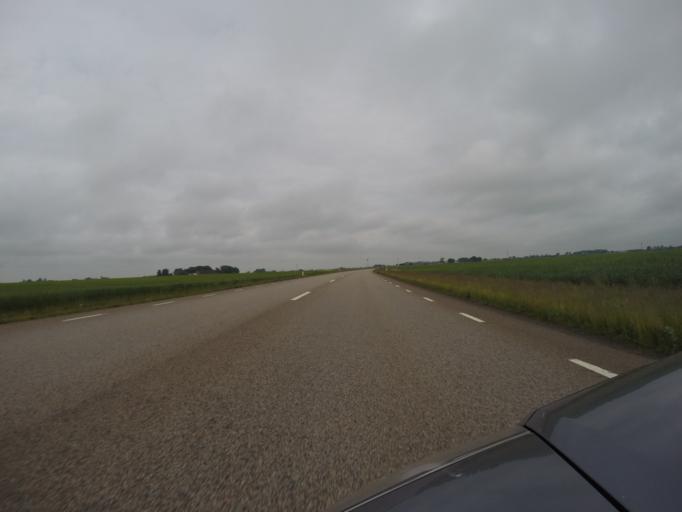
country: SE
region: Skane
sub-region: Helsingborg
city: Morarp
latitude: 56.0096
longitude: 12.9075
